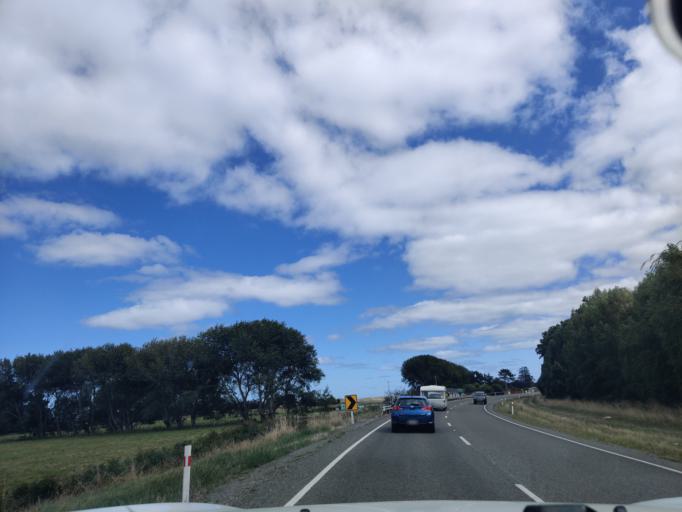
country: NZ
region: Manawatu-Wanganui
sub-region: Horowhenua District
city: Foxton
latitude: -40.4199
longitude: 175.4130
